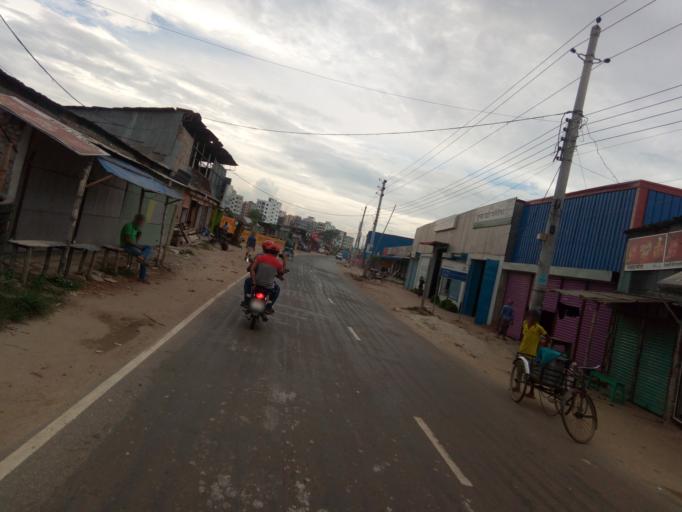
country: BD
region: Dhaka
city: Paltan
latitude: 23.7556
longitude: 90.4491
